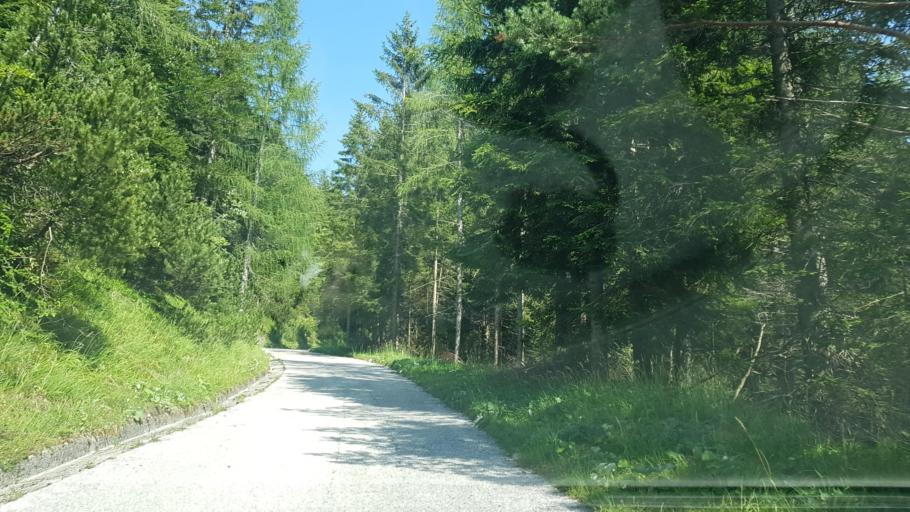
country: IT
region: Friuli Venezia Giulia
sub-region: Provincia di Udine
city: Malborghetto
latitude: 46.4631
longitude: 13.4388
